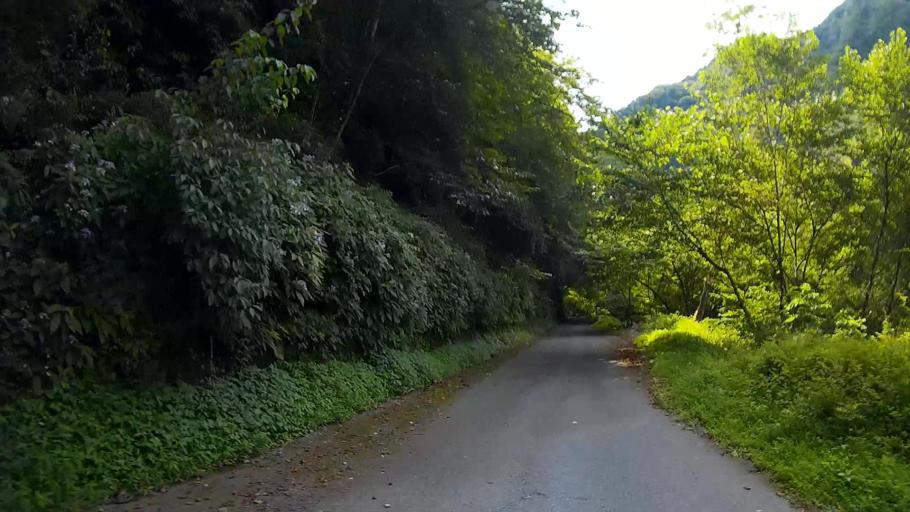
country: JP
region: Saitama
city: Chichibu
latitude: 35.8941
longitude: 139.0998
